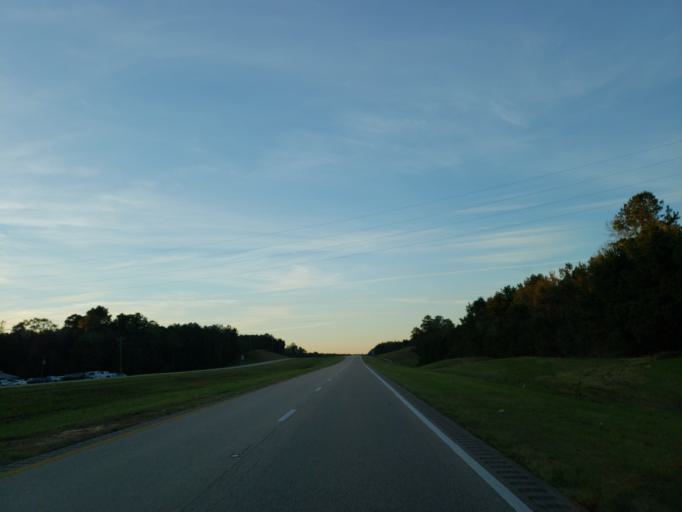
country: US
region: Mississippi
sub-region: Wayne County
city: Belmont
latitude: 31.4778
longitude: -88.4819
